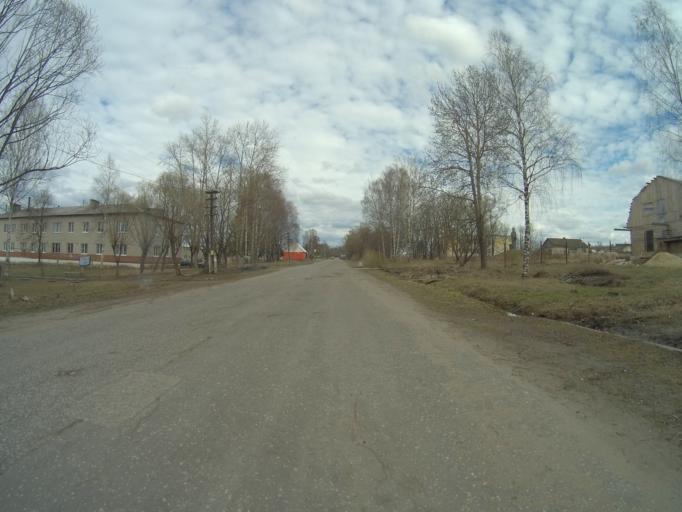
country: RU
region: Vladimir
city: Sudogda
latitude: 55.9760
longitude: 40.7315
